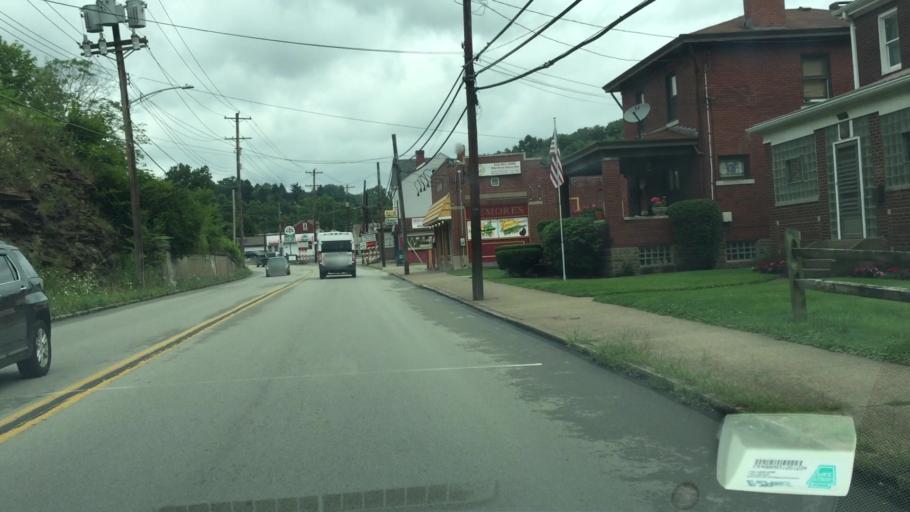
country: US
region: Pennsylvania
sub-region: Allegheny County
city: Millvale
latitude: 40.4945
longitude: -79.9759
